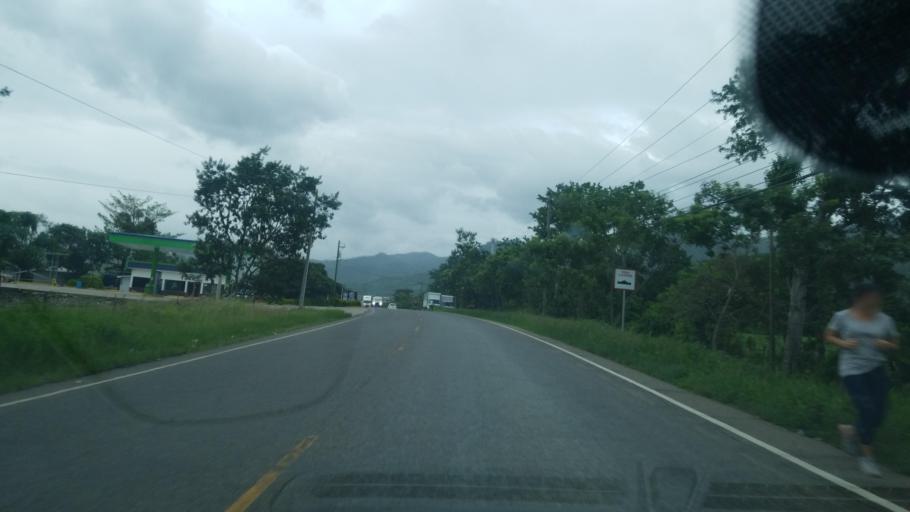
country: HN
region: Ocotepeque
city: Santa Lucia
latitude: 14.4208
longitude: -89.1883
